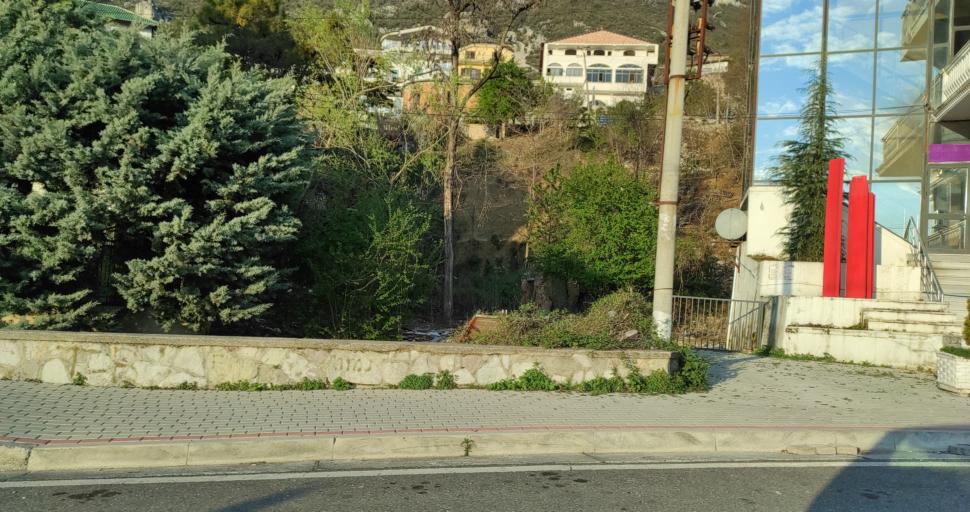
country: AL
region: Durres
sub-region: Rrethi i Krujes
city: Kruje
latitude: 41.5124
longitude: 19.7912
